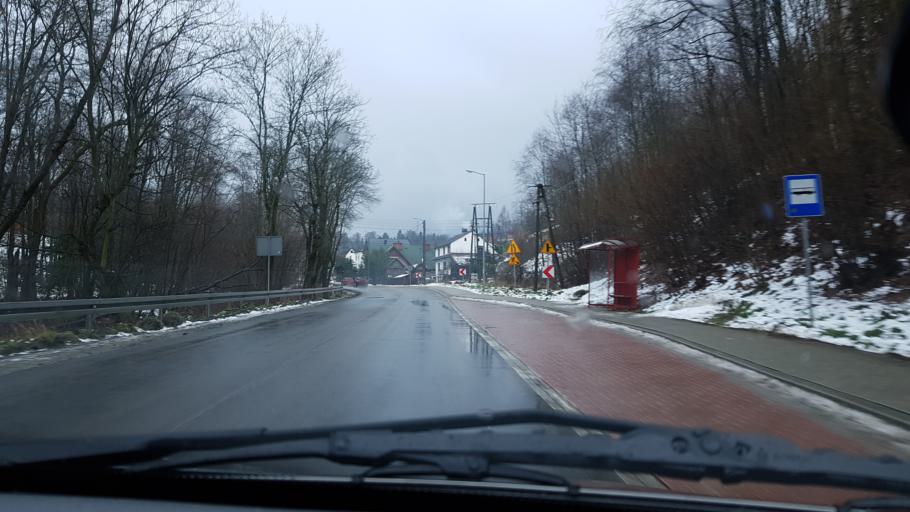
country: PL
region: Lesser Poland Voivodeship
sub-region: Powiat nowotarski
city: Raba Wyzna
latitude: 49.5419
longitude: 19.8928
